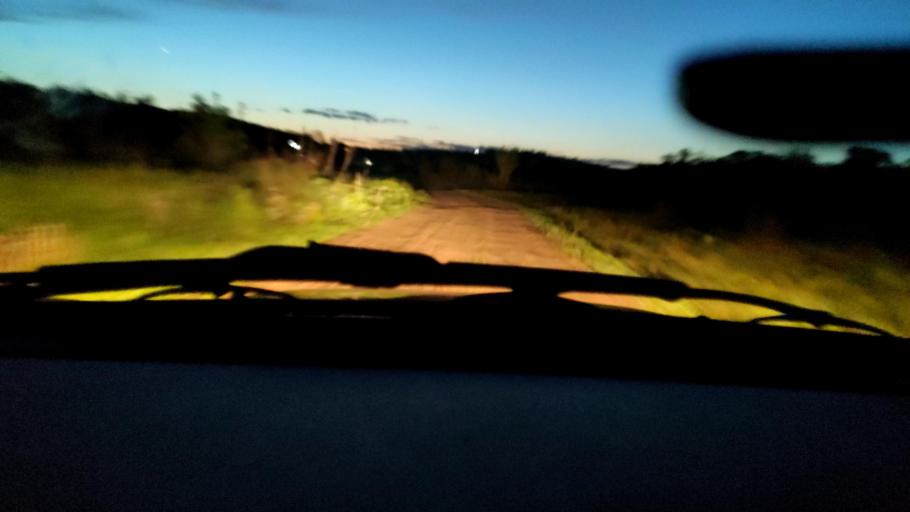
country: RU
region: Voronezj
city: Uryv-Pokrovka
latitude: 51.1021
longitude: 39.1593
